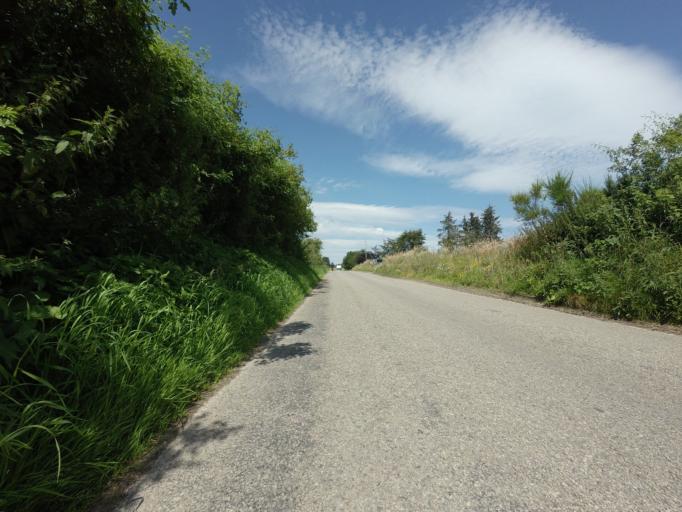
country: GB
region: Scotland
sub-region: Highland
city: Inverness
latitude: 57.5257
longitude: -4.3168
